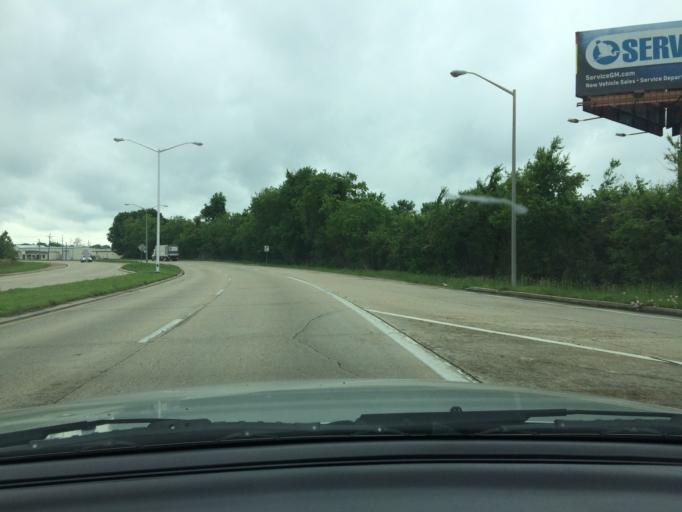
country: US
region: Louisiana
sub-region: Lafayette Parish
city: Scott
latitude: 30.2321
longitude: -92.0626
